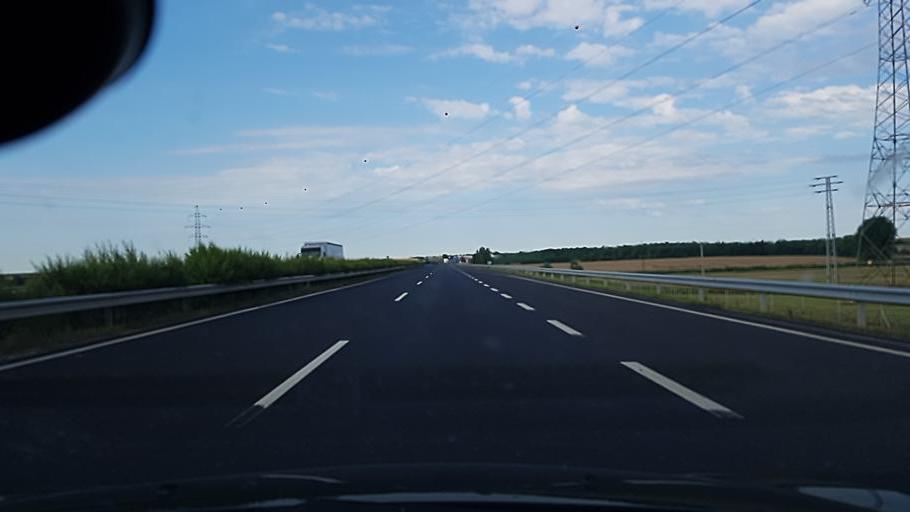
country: HU
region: Fejer
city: Rackeresztur
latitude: 47.2589
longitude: 18.8472
